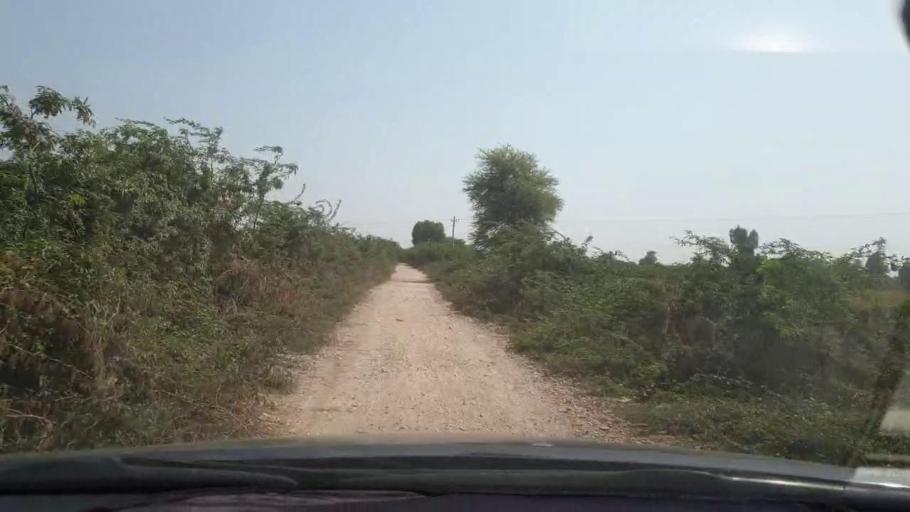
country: PK
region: Sindh
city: Naukot
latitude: 24.8113
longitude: 69.2642
